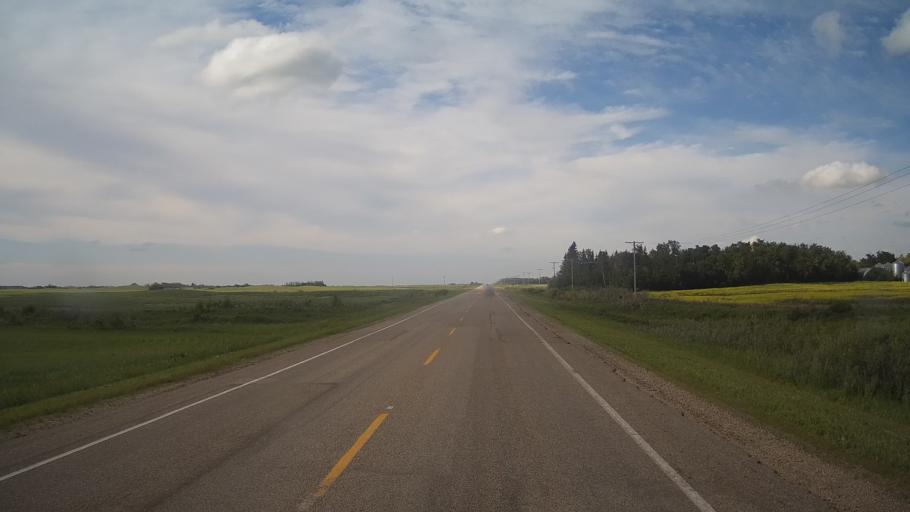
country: CA
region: Saskatchewan
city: Foam Lake
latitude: 51.6039
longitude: -103.8460
